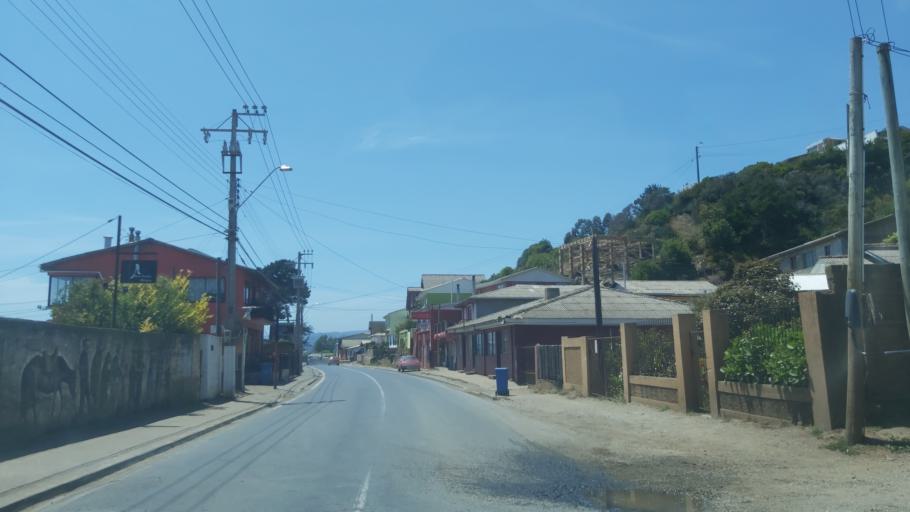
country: CL
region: Maule
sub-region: Provincia de Cauquenes
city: Cauquenes
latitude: -35.8169
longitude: -72.5854
